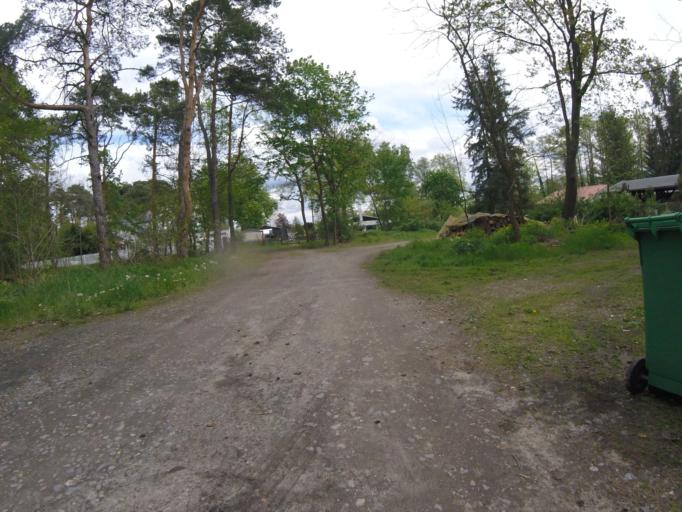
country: DE
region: Brandenburg
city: Gross Koris
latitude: 52.1650
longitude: 13.6501
